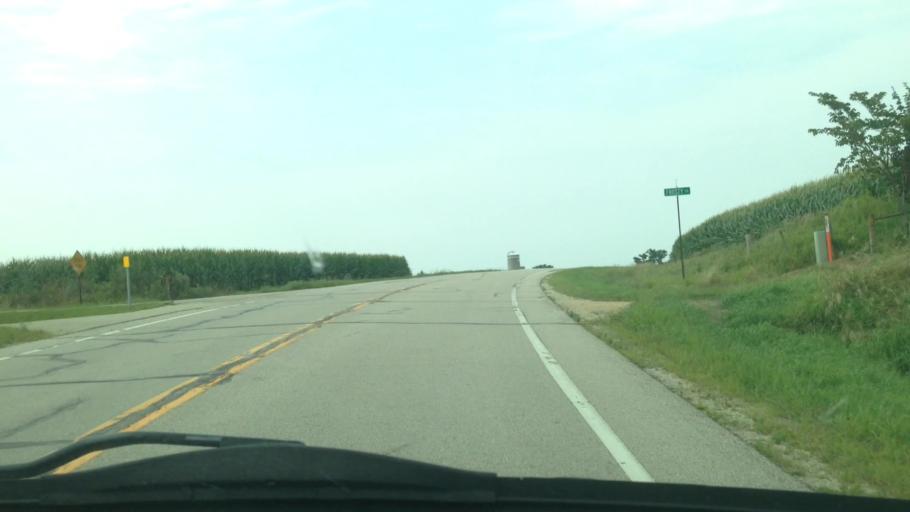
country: US
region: Minnesota
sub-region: Fillmore County
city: Preston
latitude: 43.7562
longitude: -91.9645
